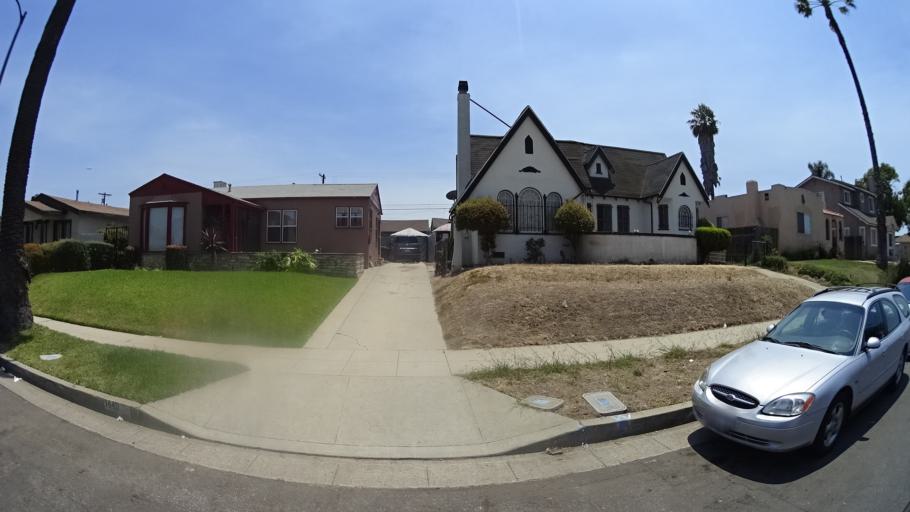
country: US
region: California
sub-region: Los Angeles County
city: Westmont
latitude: 33.9655
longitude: -118.3019
